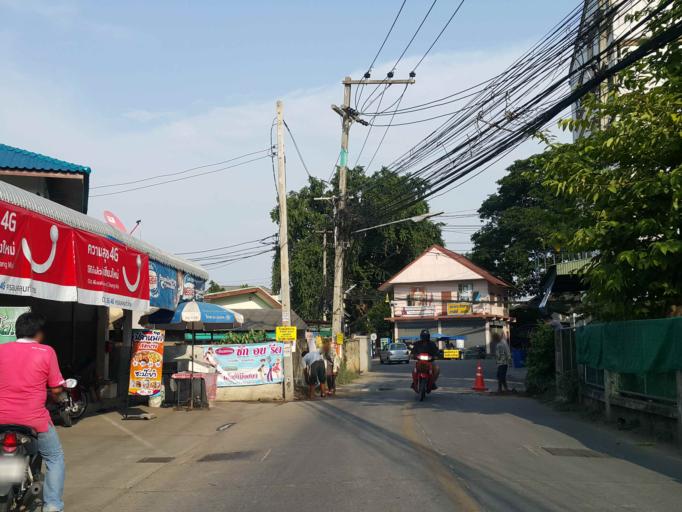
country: TH
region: Chiang Mai
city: Chiang Mai
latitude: 18.7757
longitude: 99.0201
